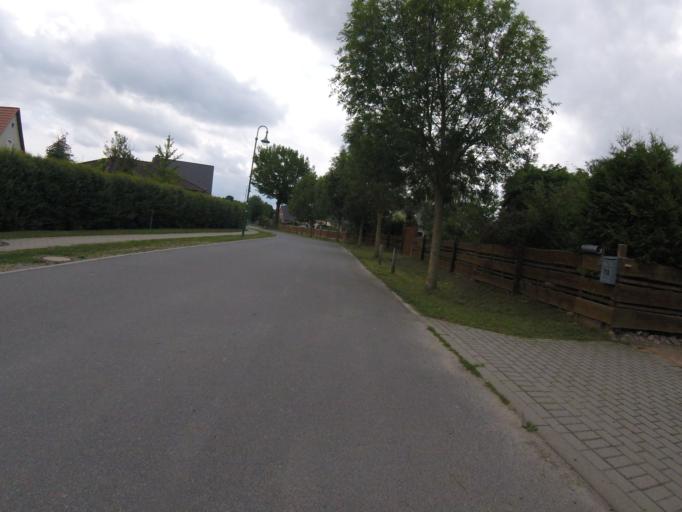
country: DE
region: Brandenburg
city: Konigs Wusterhausen
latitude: 52.2832
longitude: 13.6406
